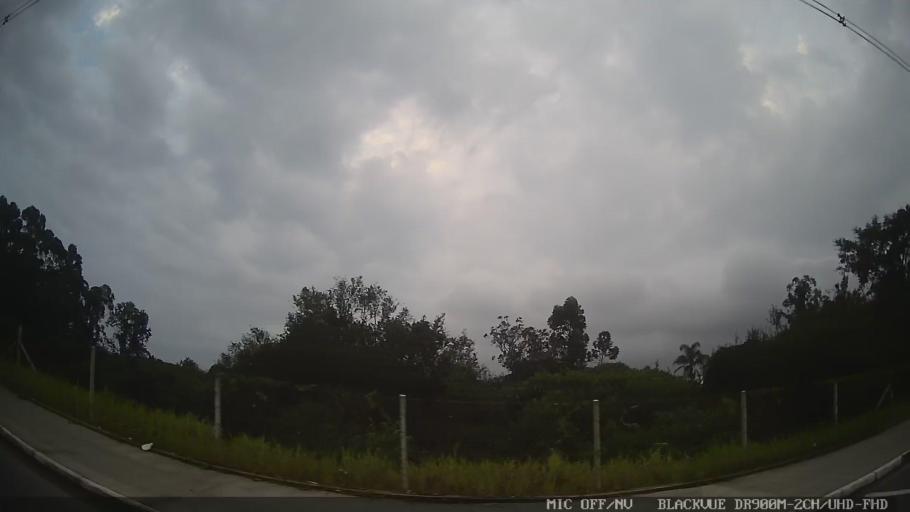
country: BR
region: Sao Paulo
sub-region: Suzano
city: Suzano
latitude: -23.5422
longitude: -46.2509
